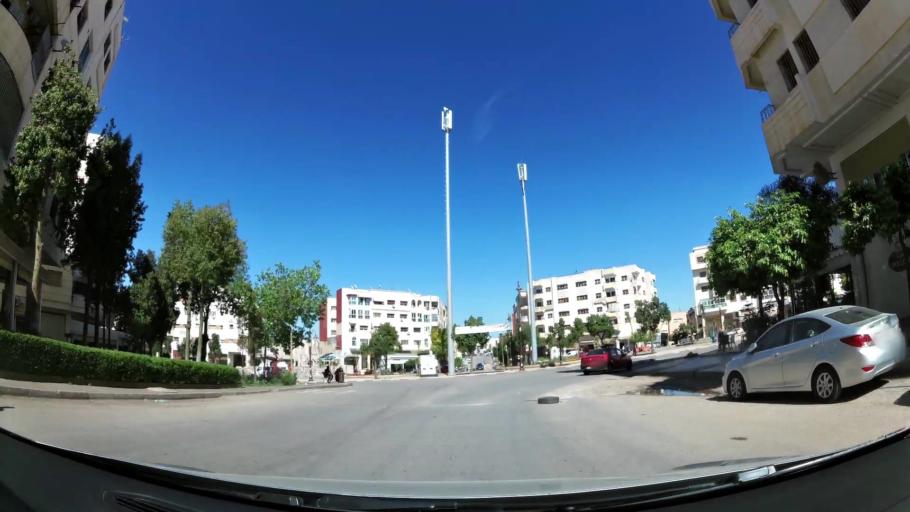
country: MA
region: Fes-Boulemane
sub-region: Fes
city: Fes
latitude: 34.0147
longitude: -4.9711
